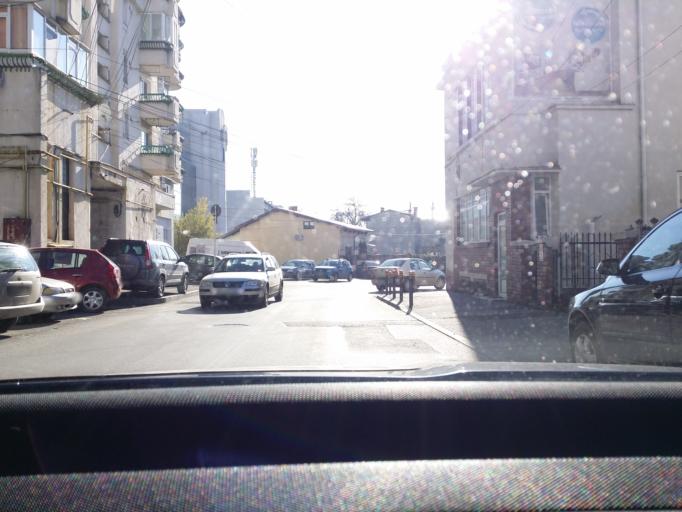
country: RO
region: Prahova
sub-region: Municipiul Campina
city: Campina
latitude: 45.1249
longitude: 25.7329
